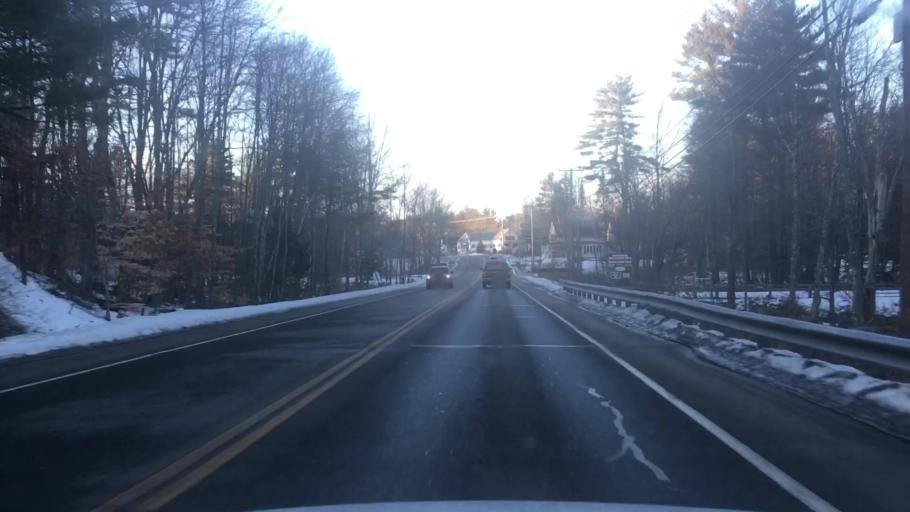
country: US
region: Maine
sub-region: York County
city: Springvale
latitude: 43.4737
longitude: -70.8104
